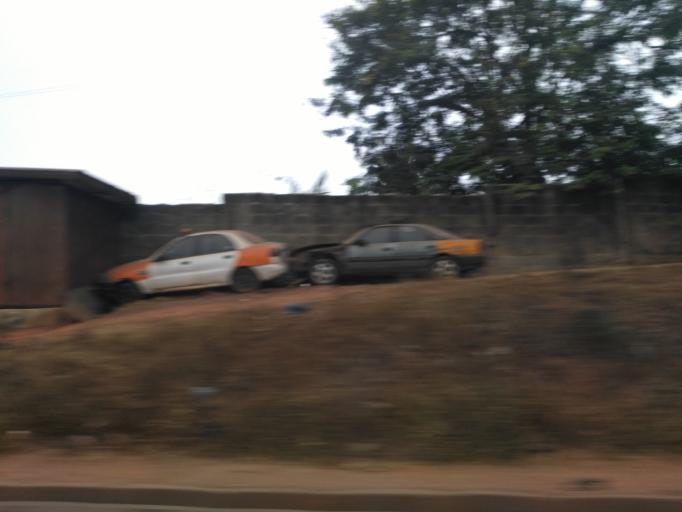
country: GH
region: Ashanti
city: Kumasi
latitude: 6.7115
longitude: -1.6229
